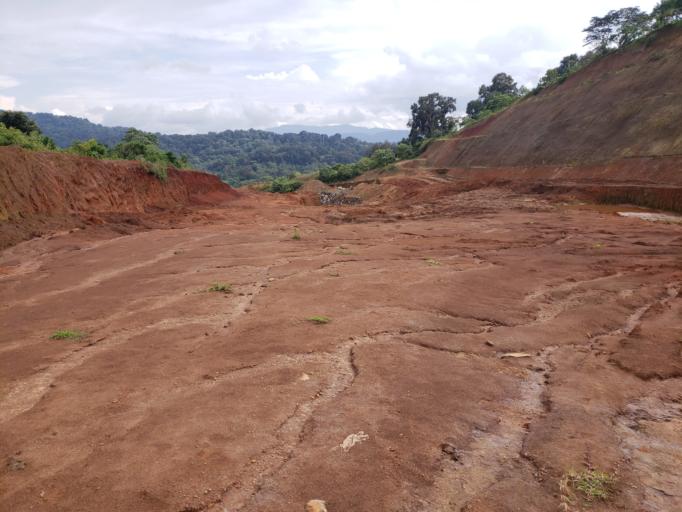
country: ET
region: Oromiya
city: Dodola
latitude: 6.5463
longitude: 39.4218
